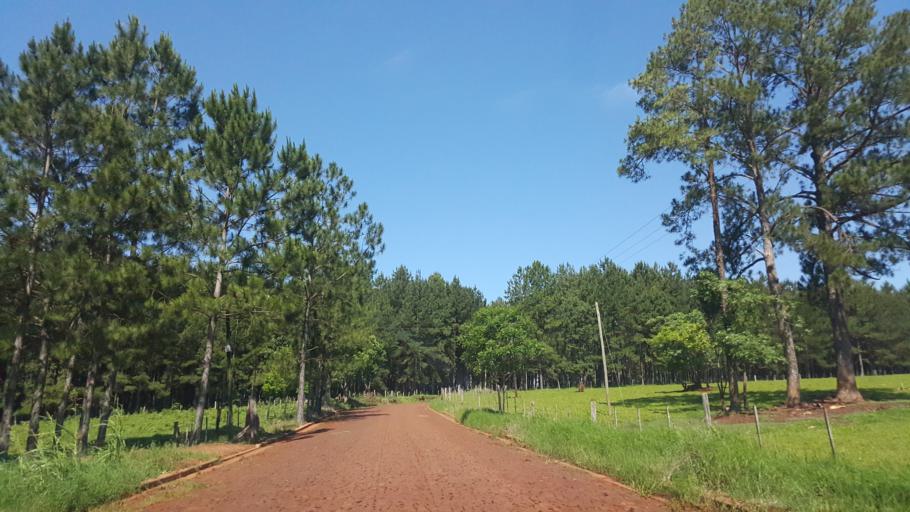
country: AR
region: Misiones
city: Capiovi
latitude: -26.9215
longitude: -55.0694
